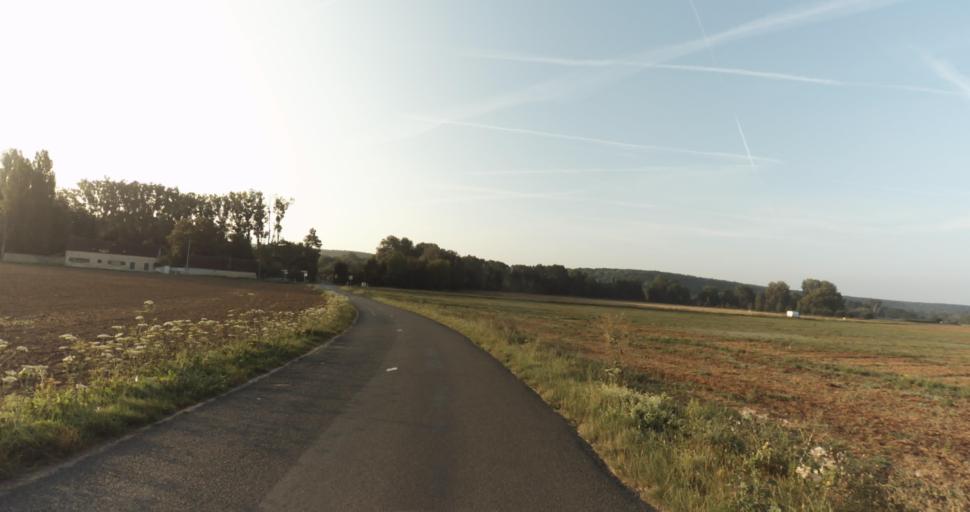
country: FR
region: Haute-Normandie
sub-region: Departement de l'Eure
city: Marcilly-sur-Eure
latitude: 48.7803
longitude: 1.3396
